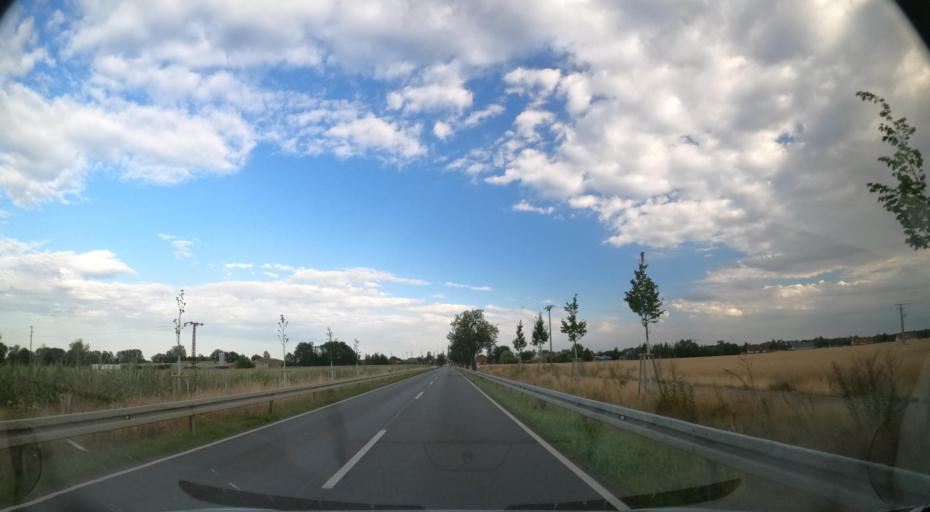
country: DE
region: Brandenburg
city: Brussow
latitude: 53.4779
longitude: 14.1183
